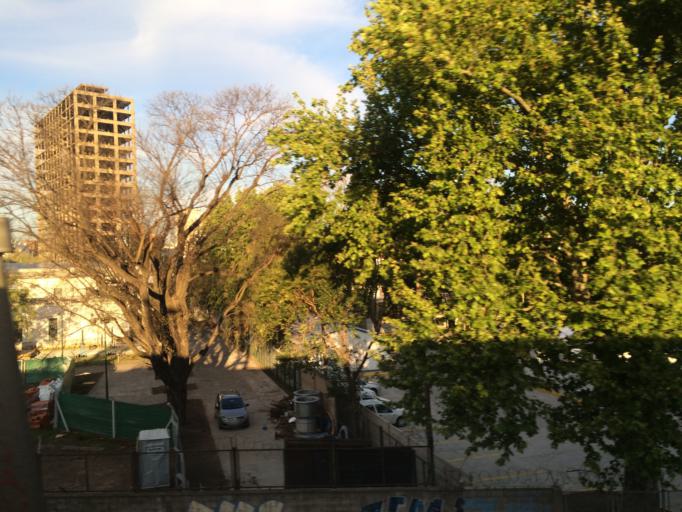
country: AR
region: Buenos Aires
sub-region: Partido de Avellaneda
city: Avellaneda
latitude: -34.6437
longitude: -58.3807
